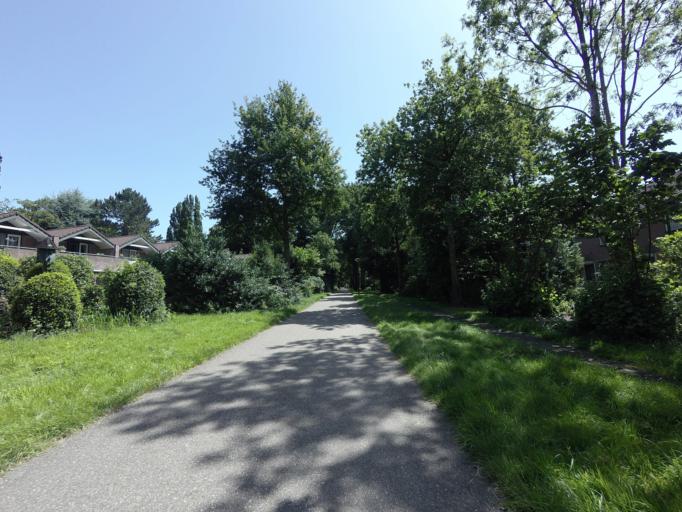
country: NL
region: Utrecht
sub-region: Gemeente De Bilt
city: De Bilt
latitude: 52.1281
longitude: 5.1849
